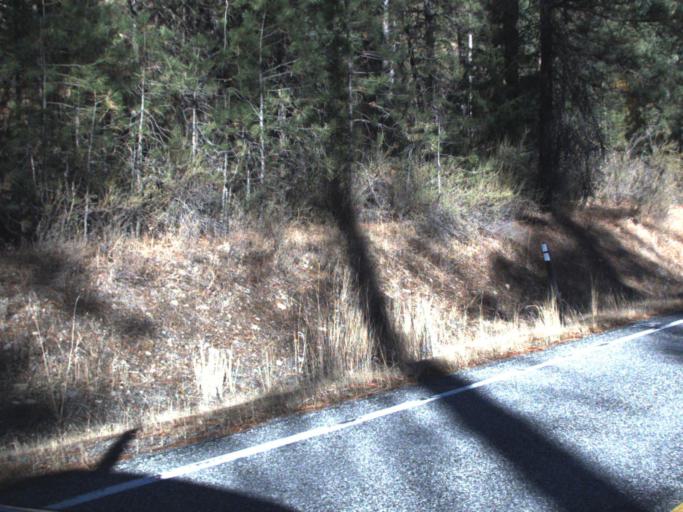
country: US
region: Washington
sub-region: Okanogan County
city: Coulee Dam
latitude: 48.0610
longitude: -118.6733
